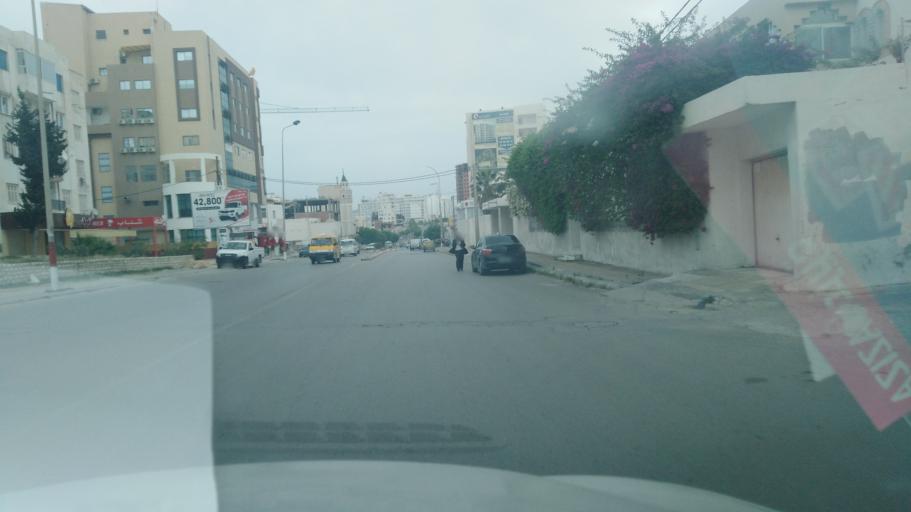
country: TN
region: Susah
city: Hammam Sousse
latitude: 35.8433
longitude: 10.6163
